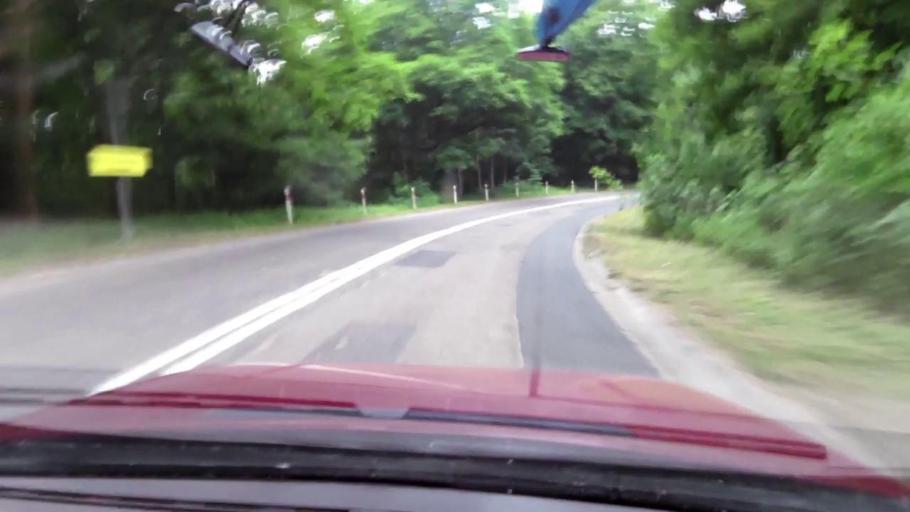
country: PL
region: West Pomeranian Voivodeship
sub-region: Powiat koszalinski
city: Sianow
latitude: 54.1863
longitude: 16.2526
